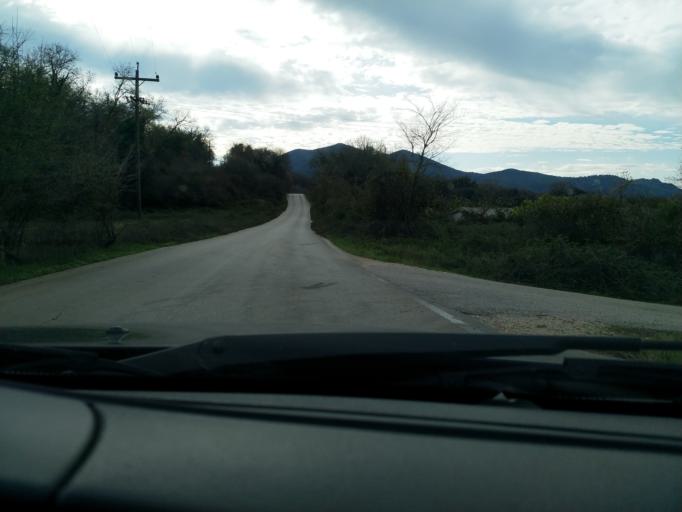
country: GR
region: Epirus
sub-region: Nomos Prevezis
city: Filippiada
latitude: 39.2289
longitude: 20.8440
